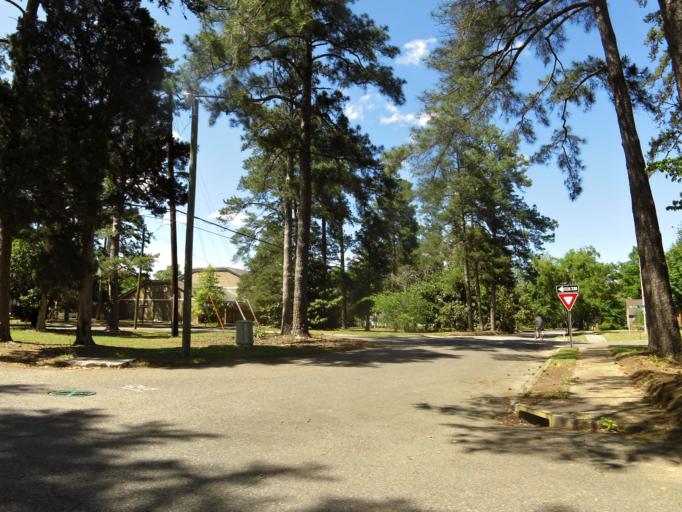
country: US
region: South Carolina
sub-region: Aiken County
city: Aiken
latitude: 33.5628
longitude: -81.7197
